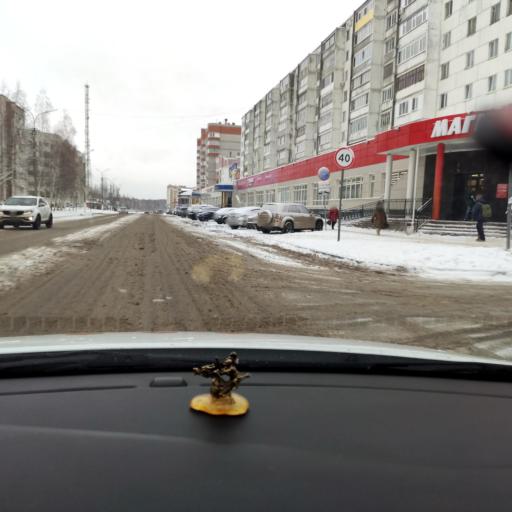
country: RU
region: Tatarstan
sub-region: Zelenodol'skiy Rayon
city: Zelenodolsk
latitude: 55.8583
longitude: 48.5646
